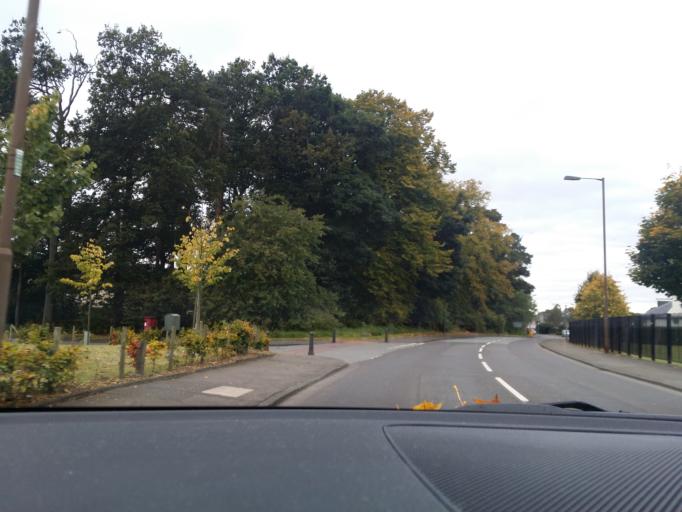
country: GB
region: Scotland
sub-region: Stirling
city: Stirling
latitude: 56.1039
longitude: -3.9486
